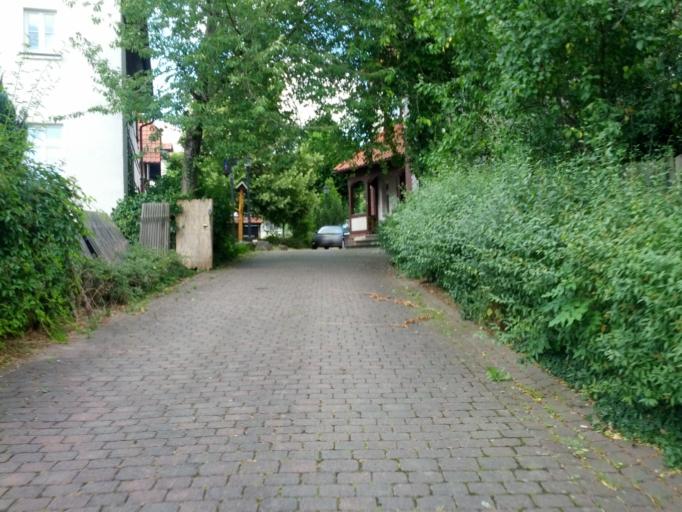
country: DE
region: Thuringia
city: Krauthausen
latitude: 50.9914
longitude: 10.2587
